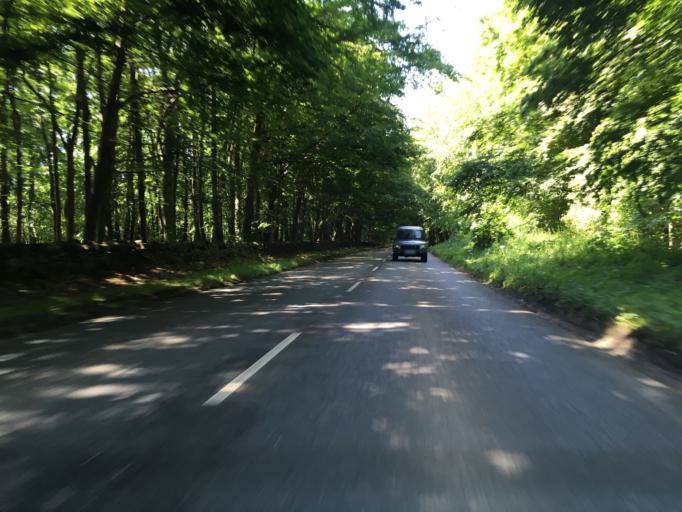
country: GB
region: England
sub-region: Oxfordshire
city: Chipping Norton
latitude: 51.9442
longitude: -1.6297
